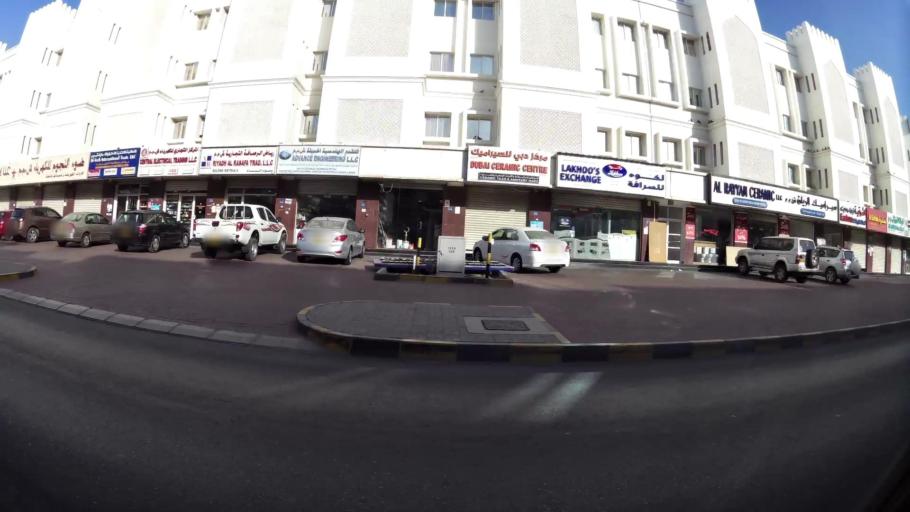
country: OM
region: Muhafazat Masqat
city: Muscat
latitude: 23.5869
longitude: 58.5505
